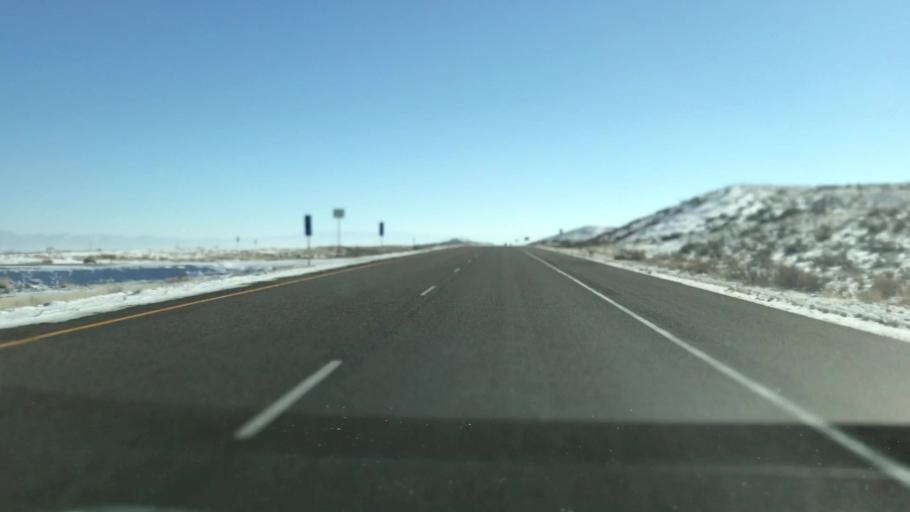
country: US
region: Colorado
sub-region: Mesa County
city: Loma
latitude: 39.2179
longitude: -108.8780
